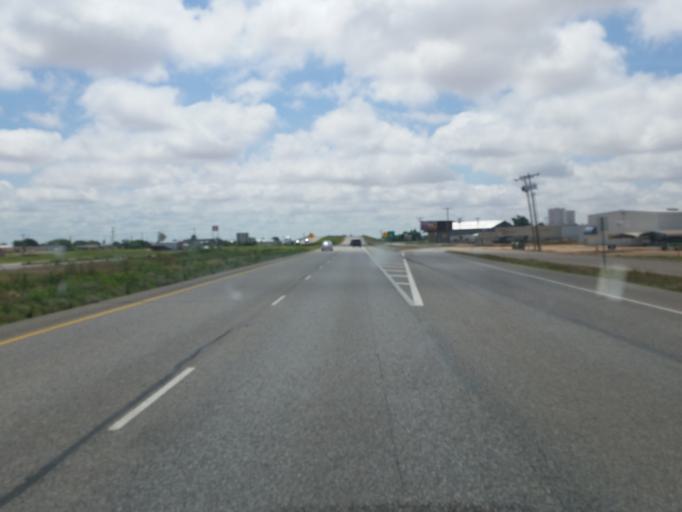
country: US
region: Texas
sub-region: Lubbock County
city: Slaton
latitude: 33.4229
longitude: -101.6481
